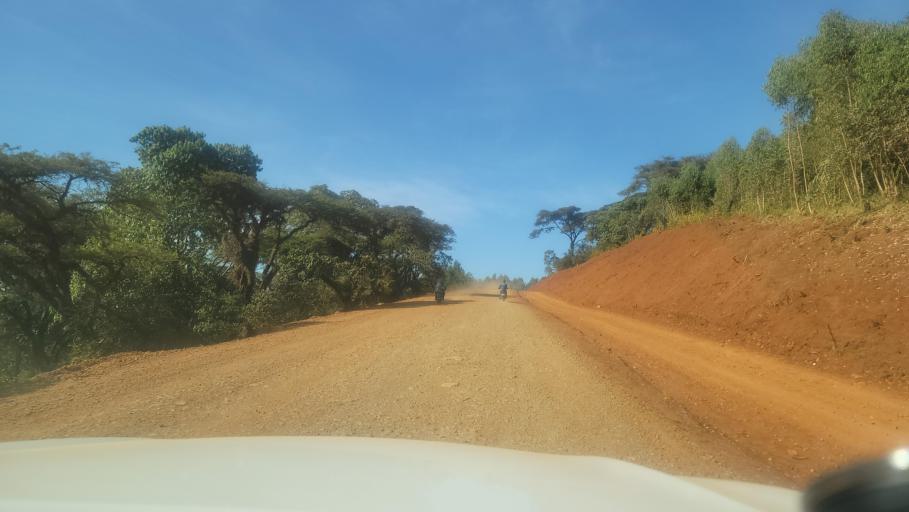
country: ET
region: Oromiya
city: Agaro
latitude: 7.8180
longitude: 36.5242
